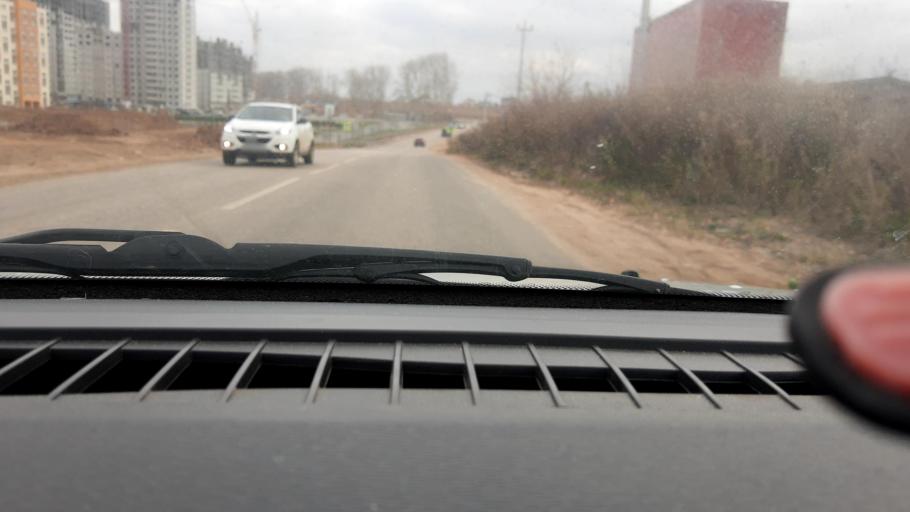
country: RU
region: Nizjnij Novgorod
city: Afonino
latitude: 56.2735
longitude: 44.0416
